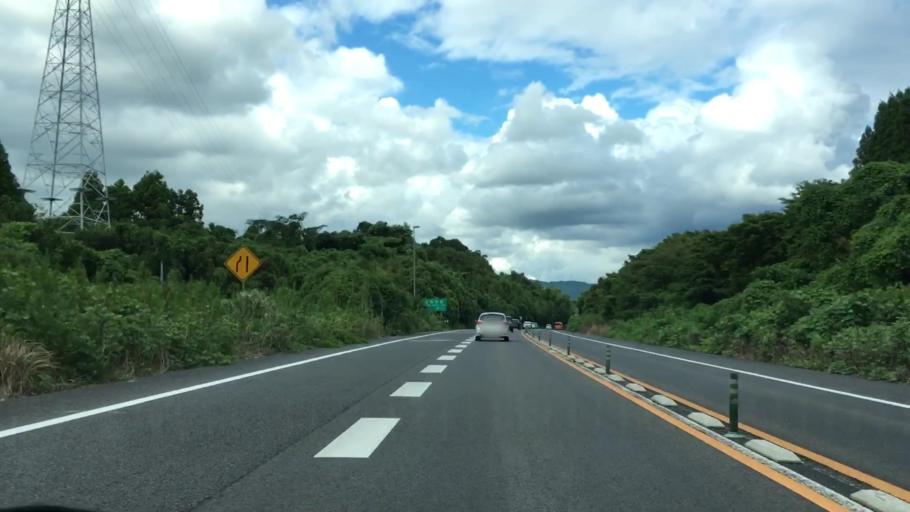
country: JP
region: Saga Prefecture
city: Karatsu
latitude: 33.4233
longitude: 130.0345
